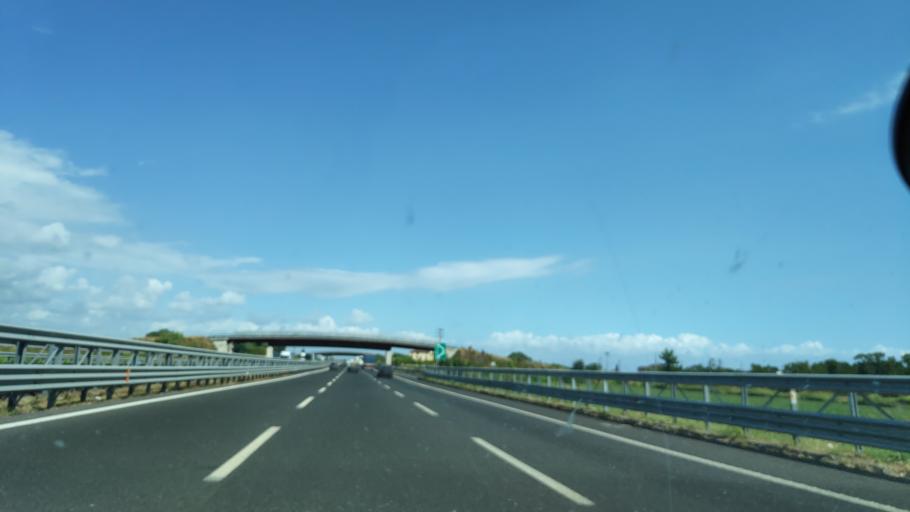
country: IT
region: Campania
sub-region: Provincia di Salerno
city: Pontecagnano
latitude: 40.6510
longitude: 14.8770
